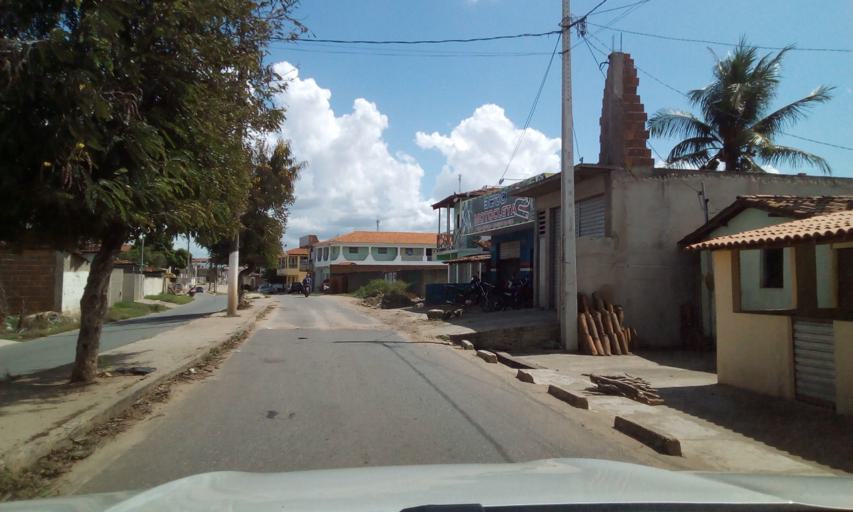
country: BR
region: Paraiba
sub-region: Guarabira
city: Guarabira
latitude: -6.8503
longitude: -35.3761
